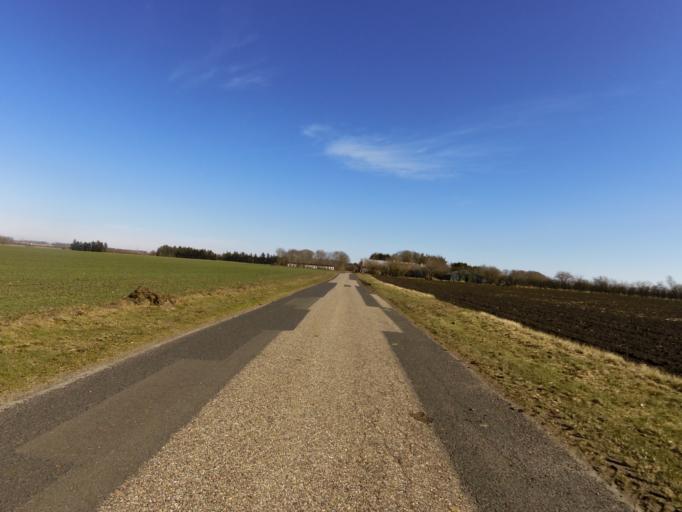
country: DK
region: South Denmark
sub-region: Tonder Kommune
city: Toftlund
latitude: 55.2369
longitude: 9.0986
